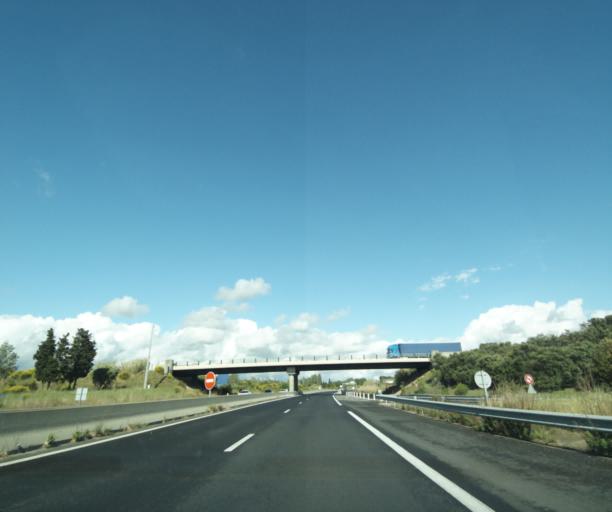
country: FR
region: Provence-Alpes-Cote d'Azur
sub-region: Departement des Bouches-du-Rhone
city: Saint-Martin-de-Crau
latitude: 43.6374
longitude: 4.8333
